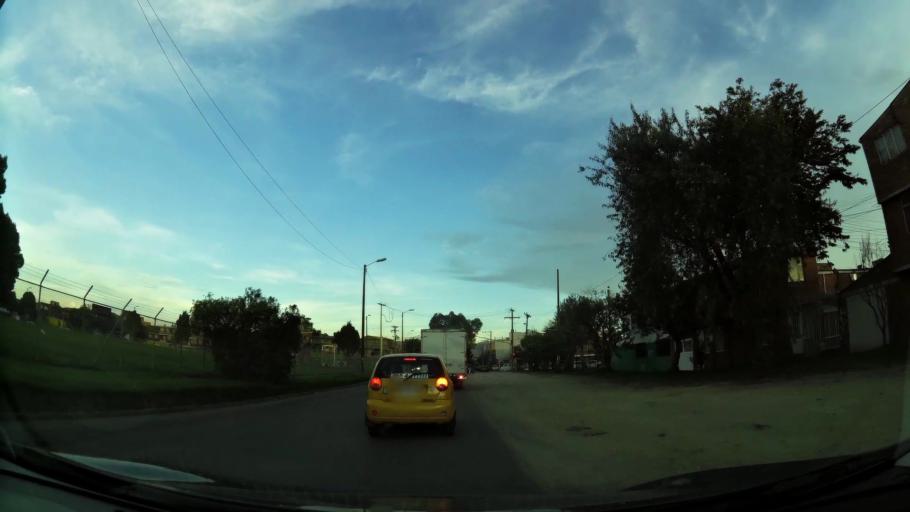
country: CO
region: Cundinamarca
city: Funza
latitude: 4.6836
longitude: -74.1364
